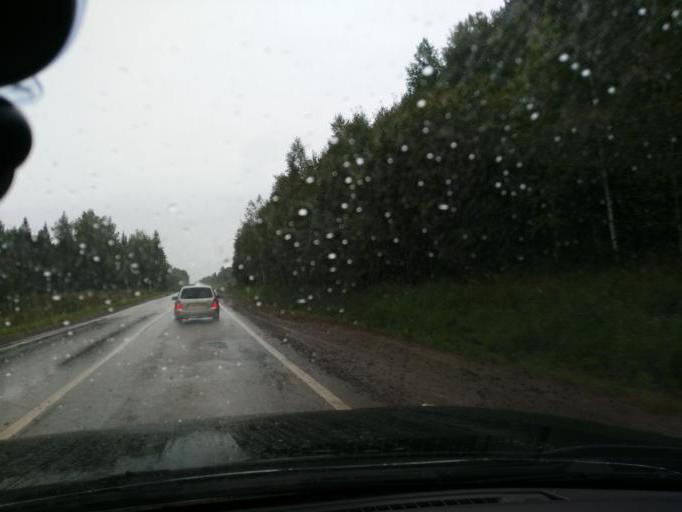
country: RU
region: Perm
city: Barda
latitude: 56.9132
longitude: 55.6799
